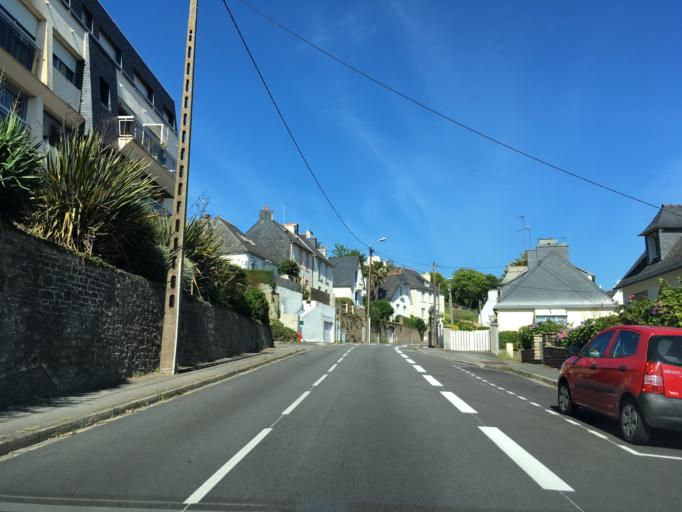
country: FR
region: Brittany
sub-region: Departement du Finistere
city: Quimper
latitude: 47.9880
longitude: -4.1064
